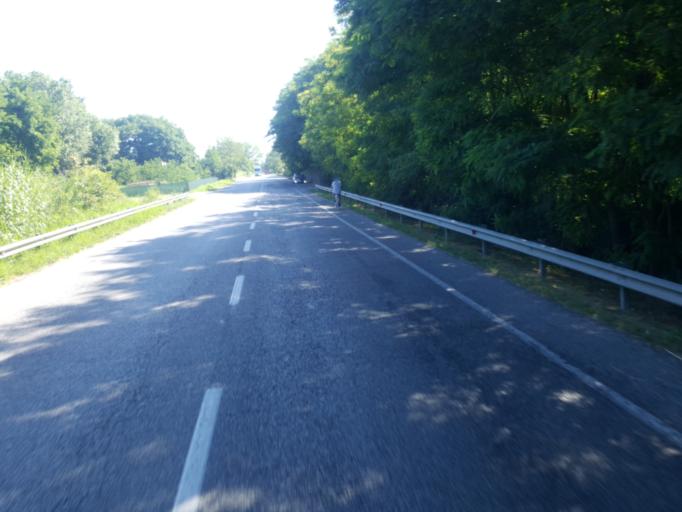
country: IT
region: The Marches
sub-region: Provincia di Pesaro e Urbino
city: Montelabbate
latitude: 43.8472
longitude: 12.7803
